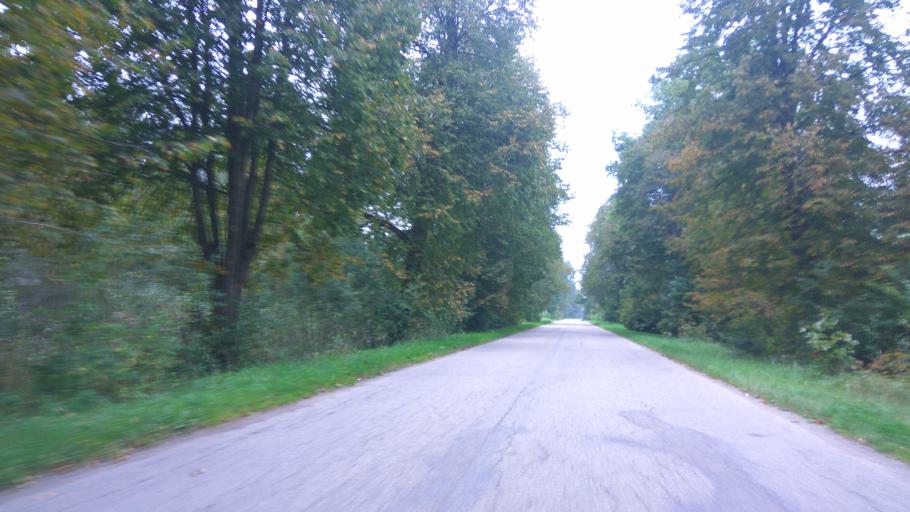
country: LV
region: Rucavas
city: Rucava
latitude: 56.1702
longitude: 21.1595
